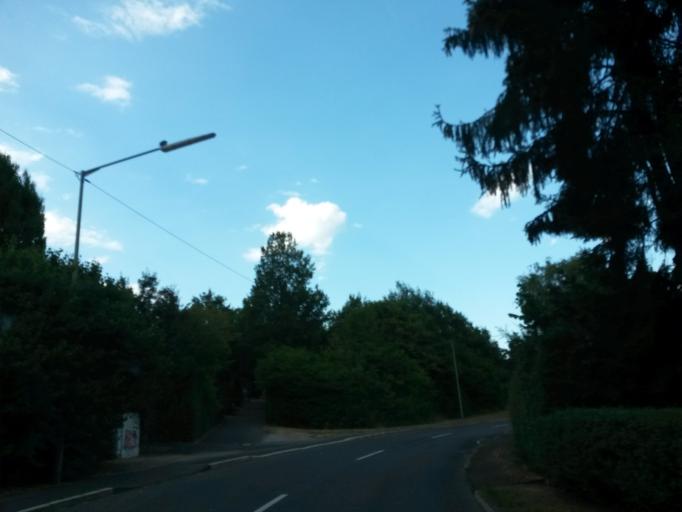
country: DE
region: North Rhine-Westphalia
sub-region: Regierungsbezirk Koln
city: Much
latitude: 50.9455
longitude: 7.4561
